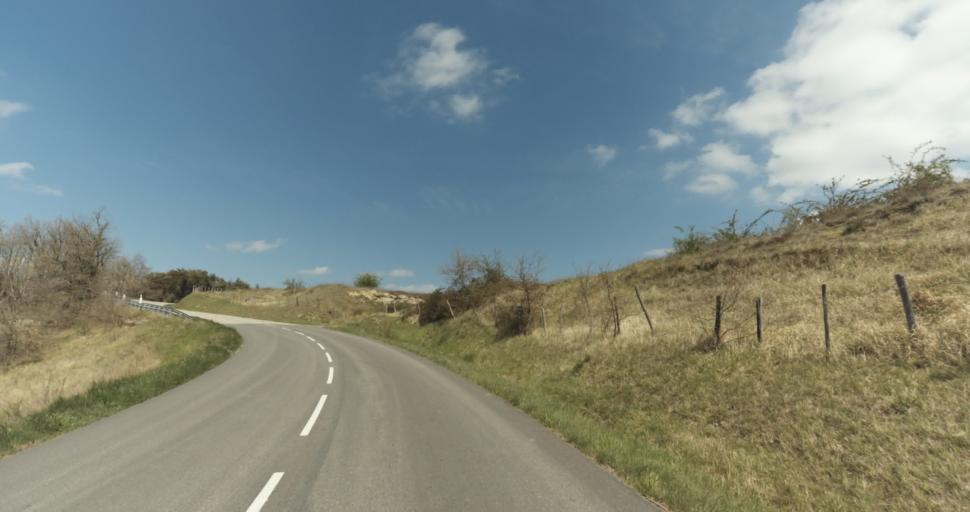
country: FR
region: Rhone-Alpes
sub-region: Departement de l'Isere
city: Saint-Verand
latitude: 45.1740
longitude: 5.3178
